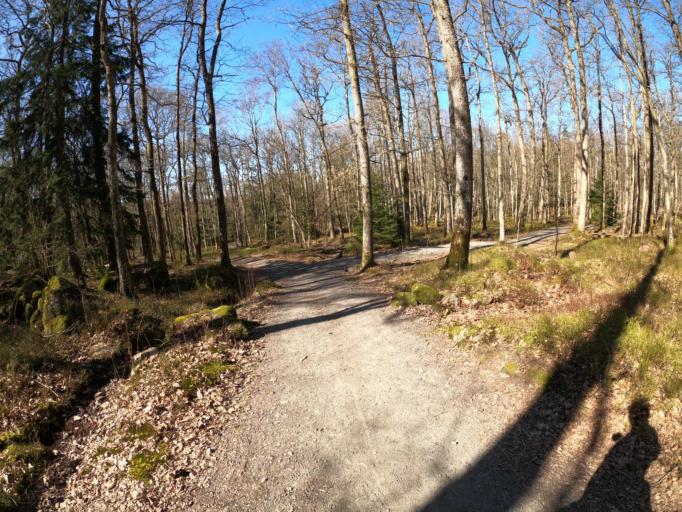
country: SE
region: Vaestra Goetaland
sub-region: Harryda Kommun
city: Molnlycke
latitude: 57.6228
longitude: 12.1118
